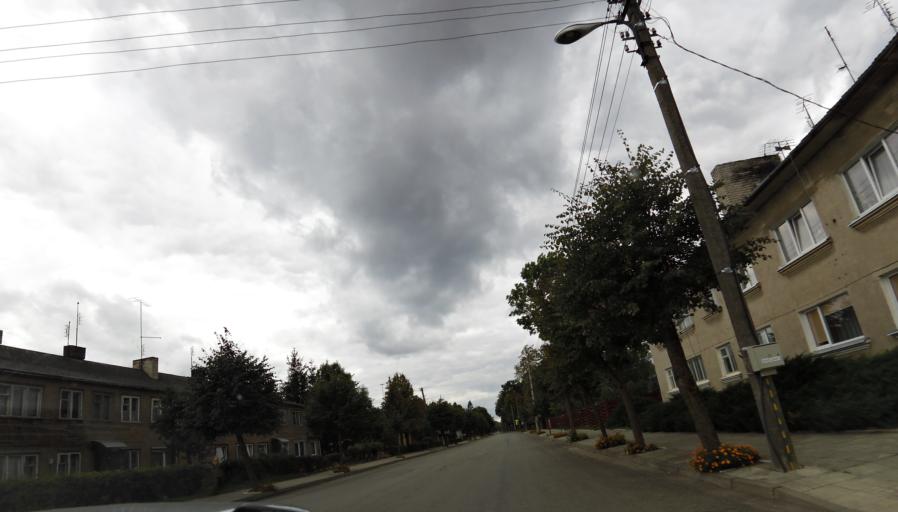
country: LT
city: Linkuva
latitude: 56.0223
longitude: 24.1679
